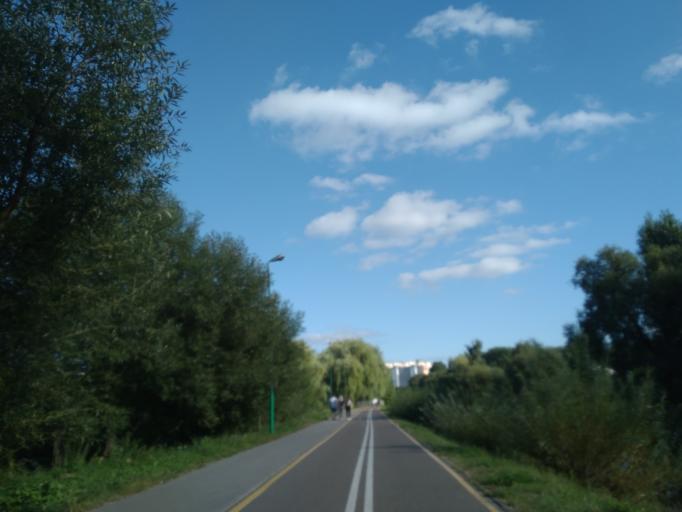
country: BY
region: Minsk
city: Minsk
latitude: 53.8714
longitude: 27.5848
